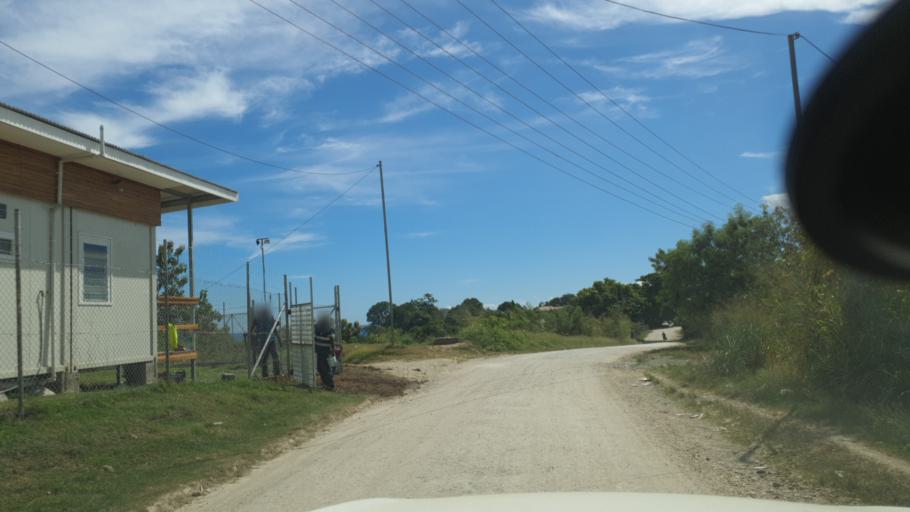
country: SB
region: Guadalcanal
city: Honiara
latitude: -9.4412
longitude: 159.9752
